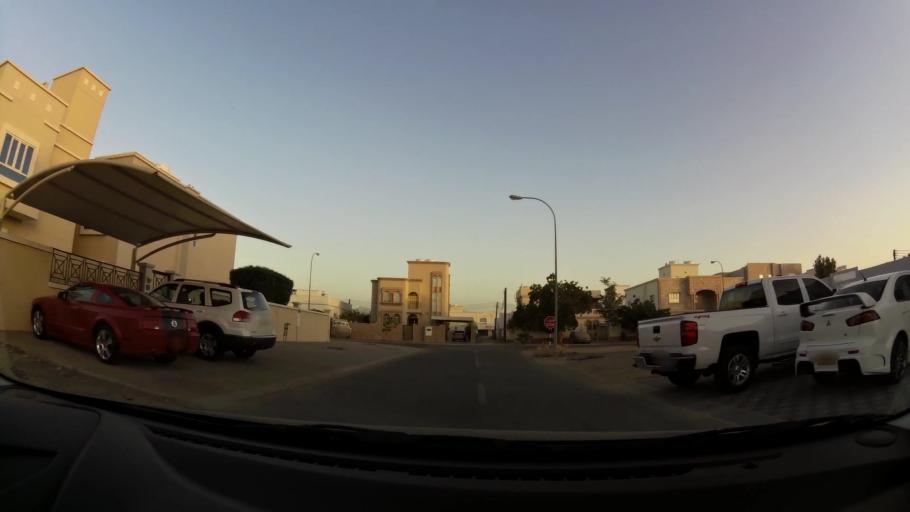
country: OM
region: Muhafazat Masqat
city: As Sib al Jadidah
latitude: 23.5942
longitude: 58.2387
